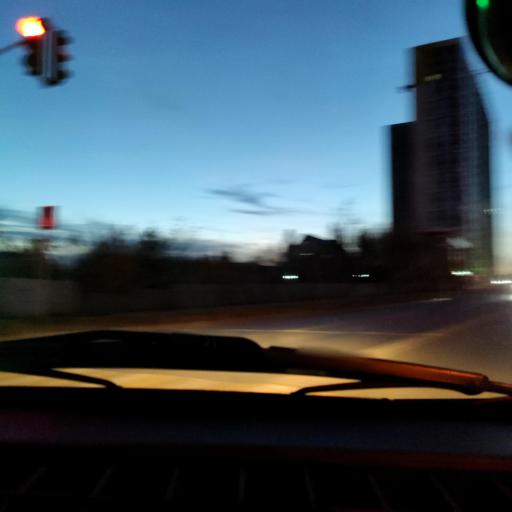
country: RU
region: Bashkortostan
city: Ufa
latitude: 54.7253
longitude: 55.9861
